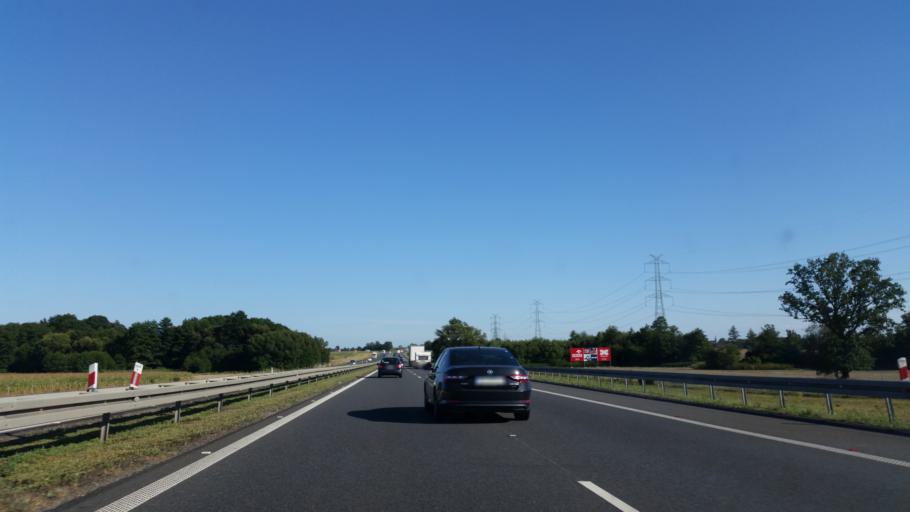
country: PL
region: Lower Silesian Voivodeship
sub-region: Powiat strzelinski
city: Wiazow
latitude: 50.8242
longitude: 17.2978
